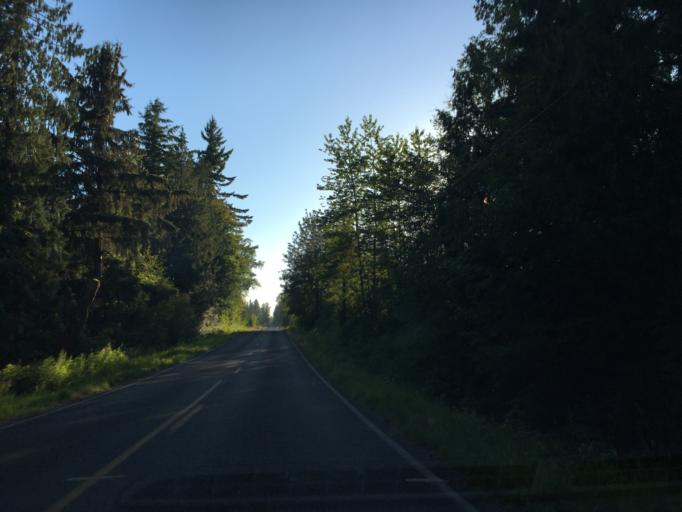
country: US
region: Washington
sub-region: Whatcom County
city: Geneva
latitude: 48.8184
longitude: -122.3727
